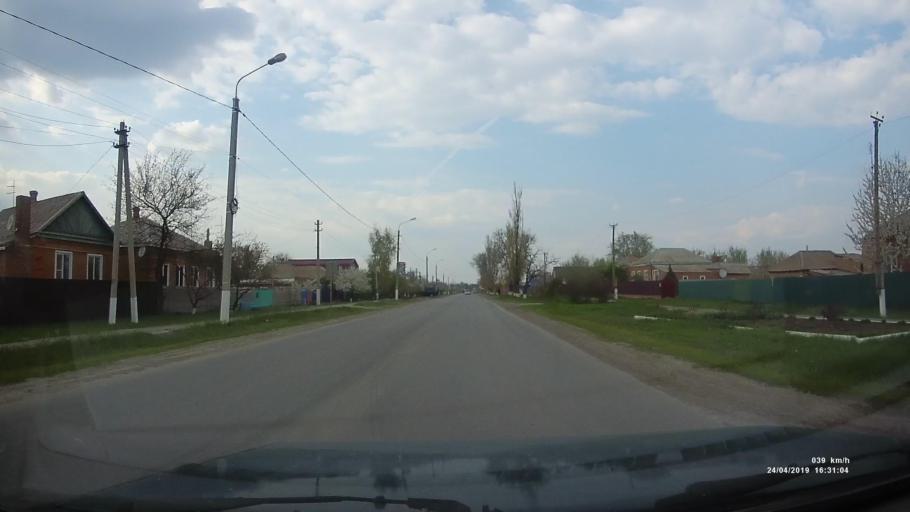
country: RU
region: Rostov
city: Orlovskiy
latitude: 46.8783
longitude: 42.0384
